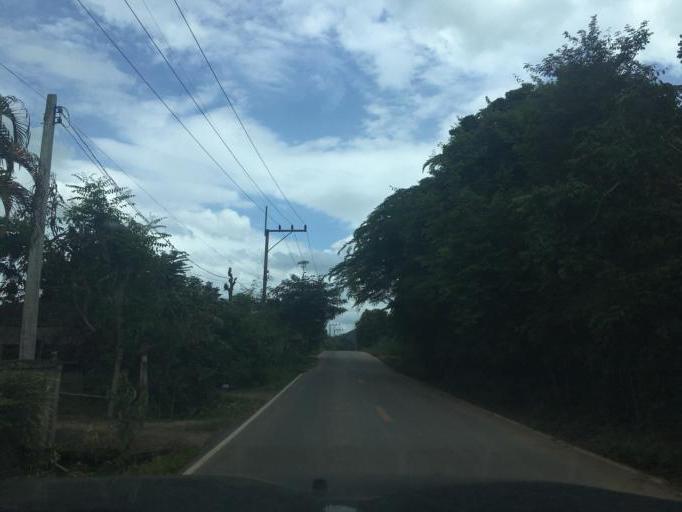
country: TH
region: Chiang Rai
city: Wiang Pa Pao
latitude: 19.2332
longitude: 99.4908
